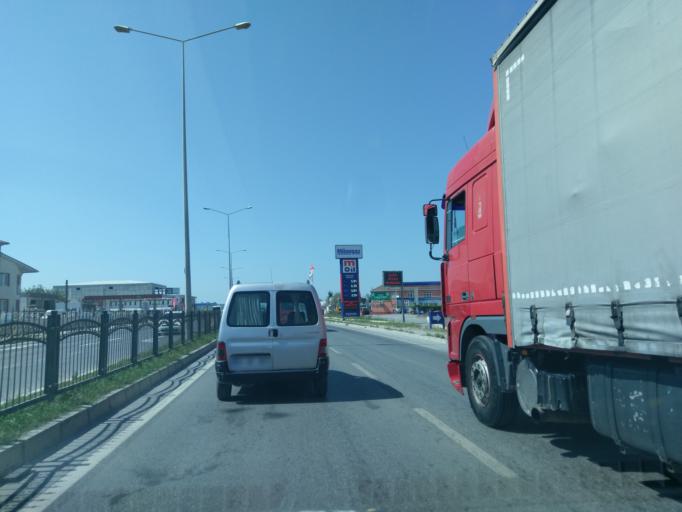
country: TR
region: Samsun
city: Bafra
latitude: 41.5653
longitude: 35.8856
